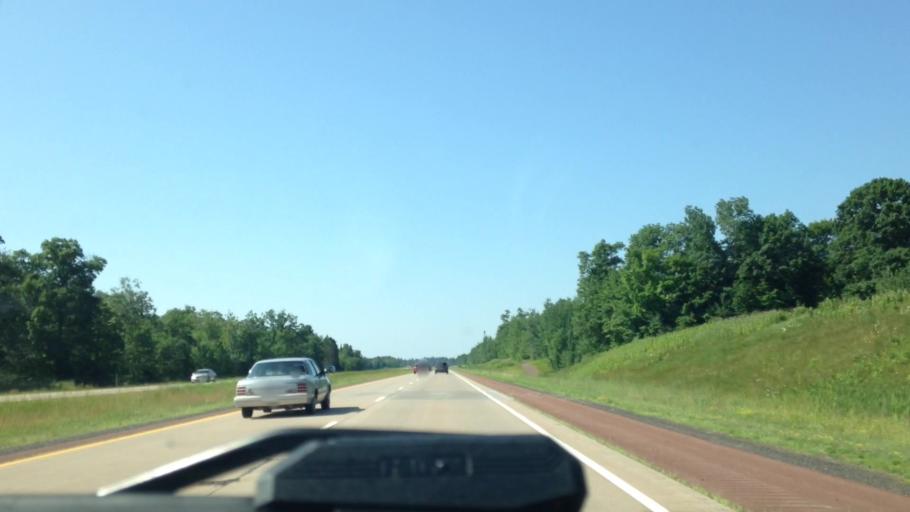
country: US
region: Wisconsin
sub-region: Douglas County
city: Lake Nebagamon
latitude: 46.3738
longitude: -91.8265
